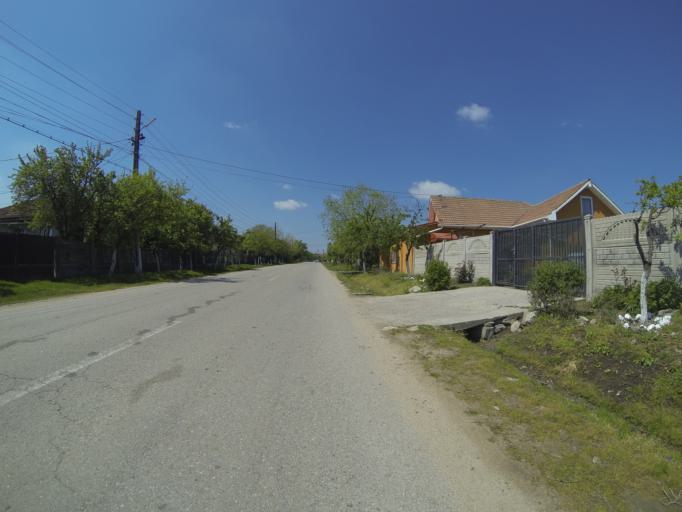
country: RO
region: Dolj
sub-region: Comuna Breasta
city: Breasta
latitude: 44.2989
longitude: 23.6511
